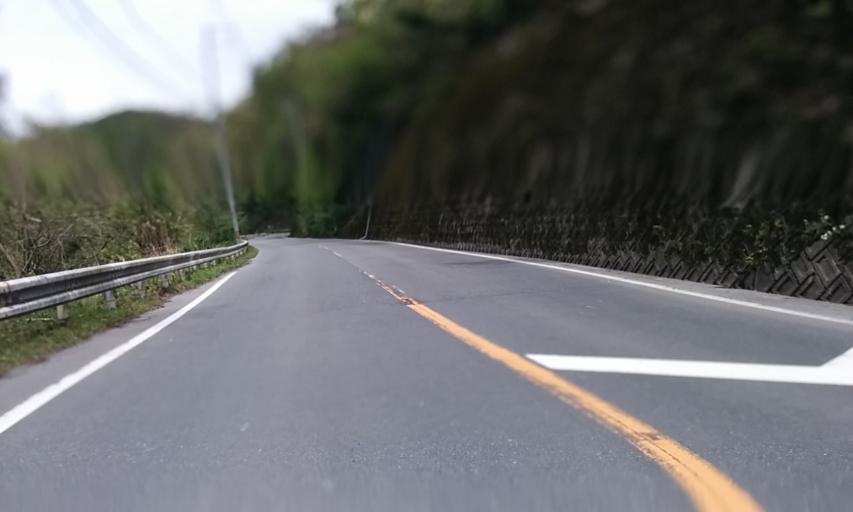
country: JP
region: Kyoto
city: Kameoka
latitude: 34.9311
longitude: 135.6010
